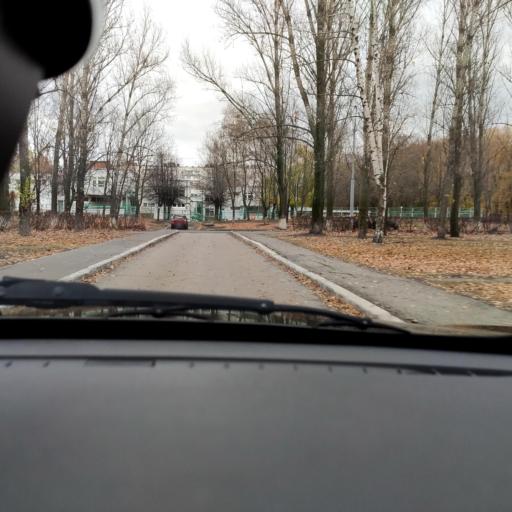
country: RU
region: Samara
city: Tol'yatti
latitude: 53.5255
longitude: 49.2902
